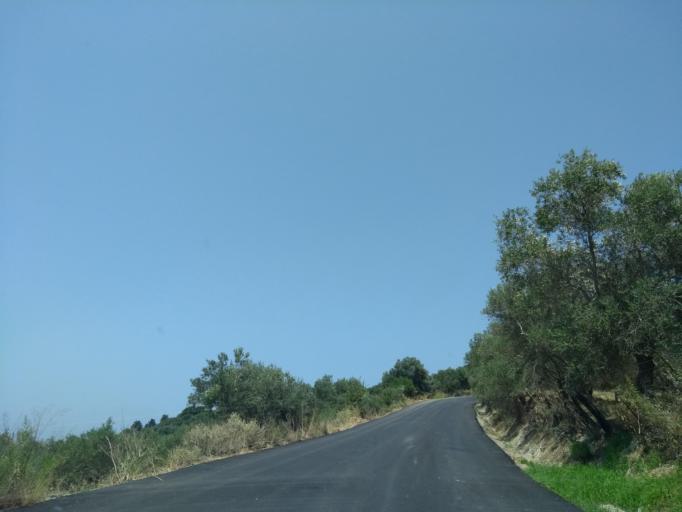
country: GR
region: Crete
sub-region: Nomos Chanias
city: Georgioupolis
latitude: 35.3280
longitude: 24.2991
